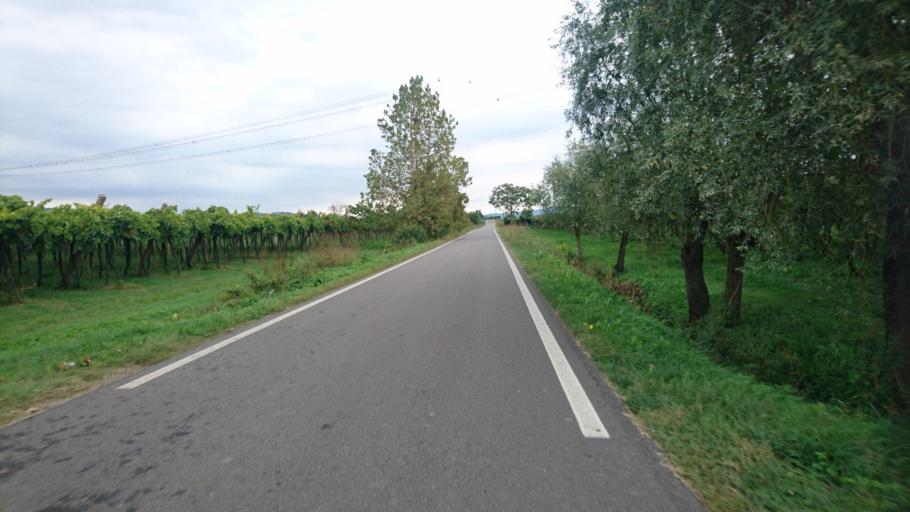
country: IT
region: Veneto
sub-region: Provincia di Verona
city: Locara
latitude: 45.4286
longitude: 11.3207
